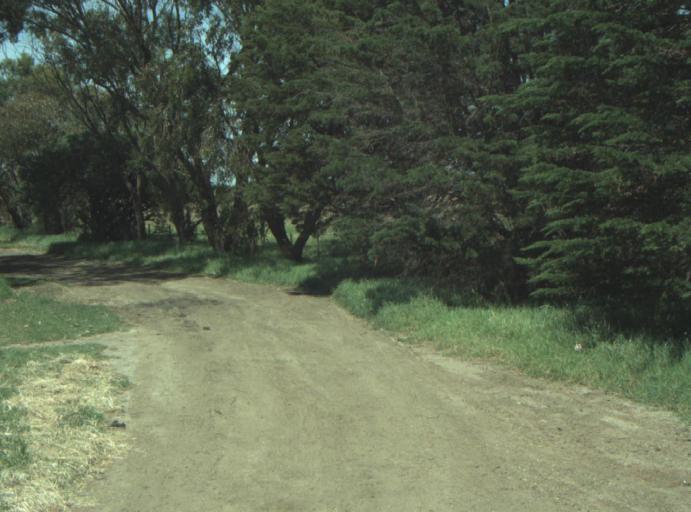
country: AU
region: Victoria
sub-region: Greater Geelong
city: Leopold
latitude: -38.1644
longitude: 144.4731
